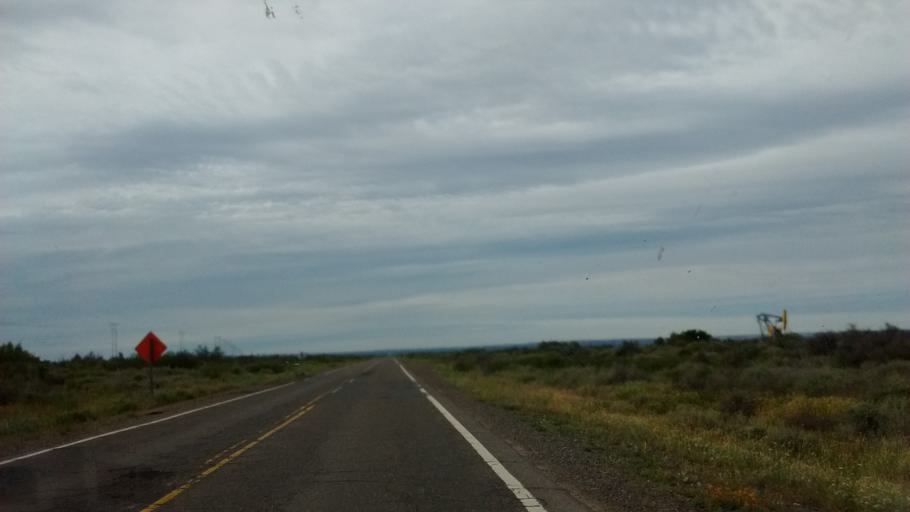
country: AR
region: Rio Negro
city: Catriel
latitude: -37.9842
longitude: -67.9088
